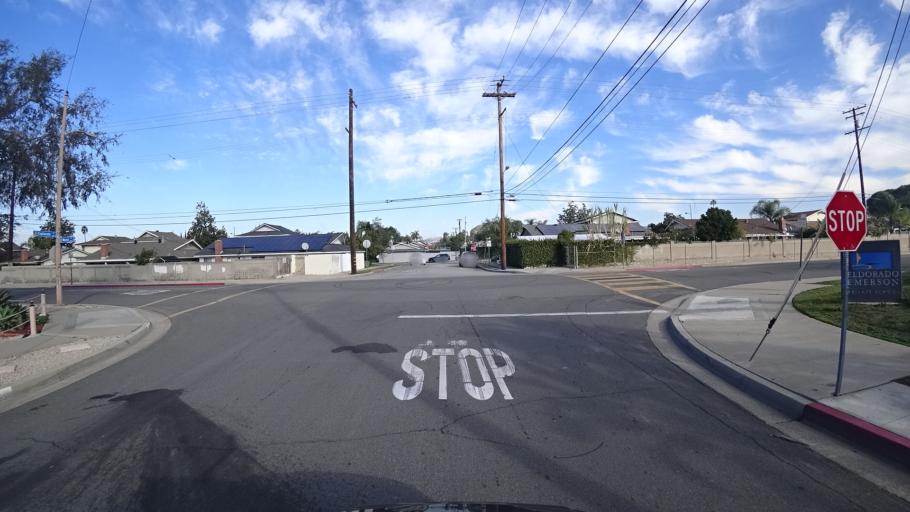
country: US
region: California
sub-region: Orange County
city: Villa Park
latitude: 33.7949
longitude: -117.8101
